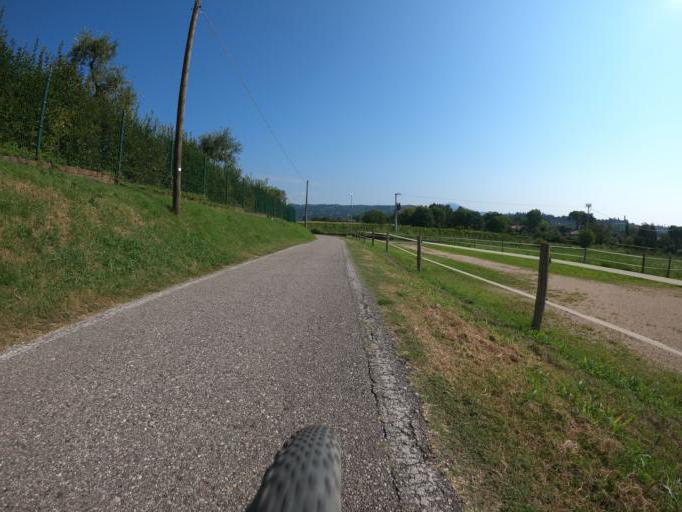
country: IT
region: Veneto
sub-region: Provincia di Verona
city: Calmasino
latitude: 45.5220
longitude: 10.7354
